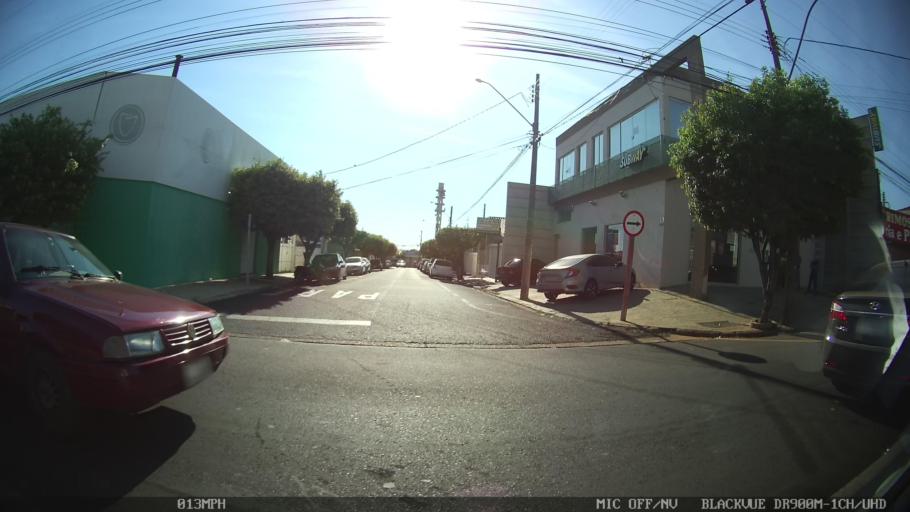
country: BR
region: Sao Paulo
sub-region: Sao Jose Do Rio Preto
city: Sao Jose do Rio Preto
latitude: -20.7971
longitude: -49.3659
